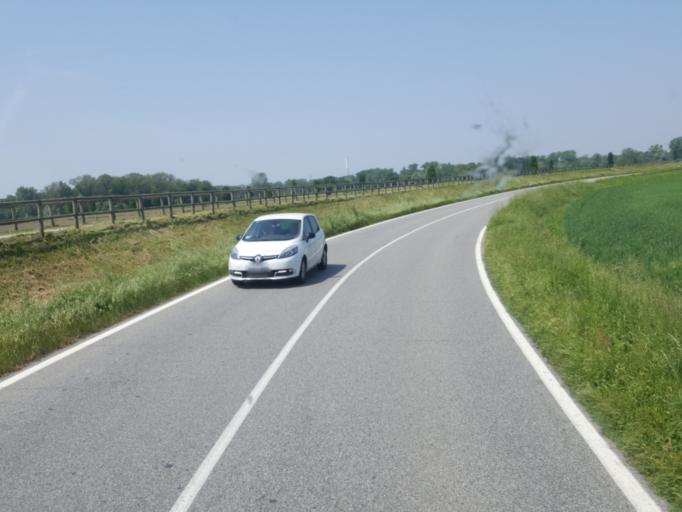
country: IT
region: Lombardy
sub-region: Provincia di Lodi
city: Lodi
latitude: 45.3309
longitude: 9.5061
